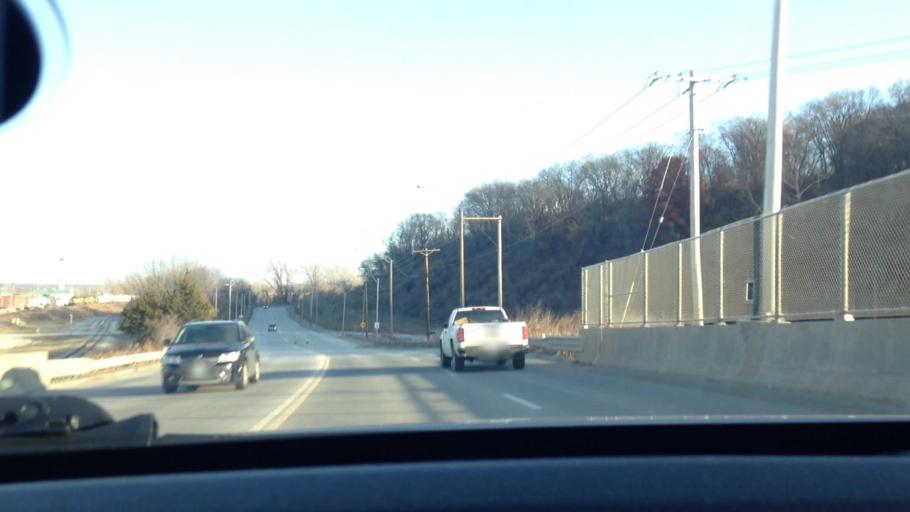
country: US
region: Missouri
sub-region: Clay County
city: North Kansas City
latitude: 39.1213
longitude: -94.5132
